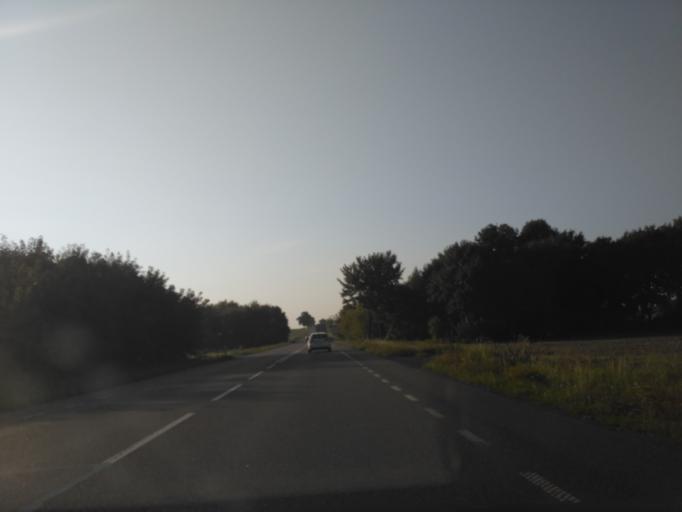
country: PL
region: Lublin Voivodeship
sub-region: Powiat janowski
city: Modliborzyce
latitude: 50.7338
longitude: 22.3558
